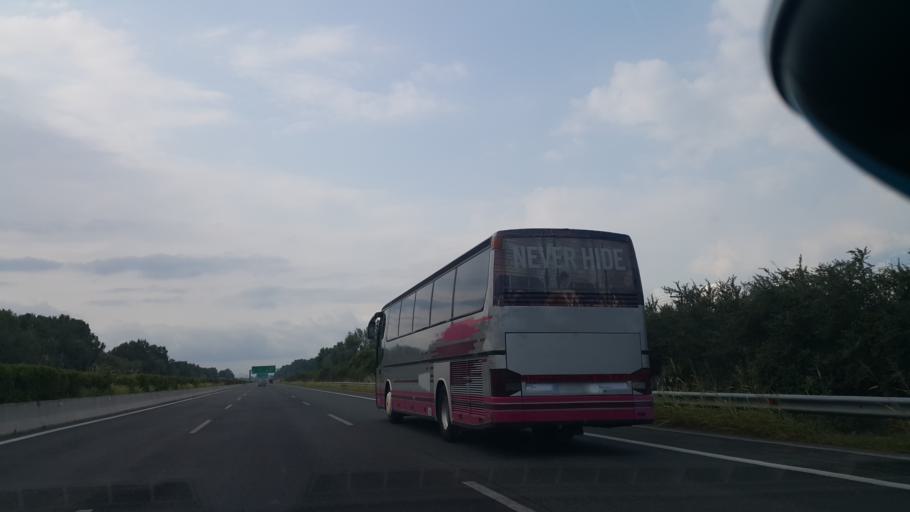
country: GR
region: Central Macedonia
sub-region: Nomos Pierias
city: Nea Efesos
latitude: 40.2109
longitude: 22.5442
